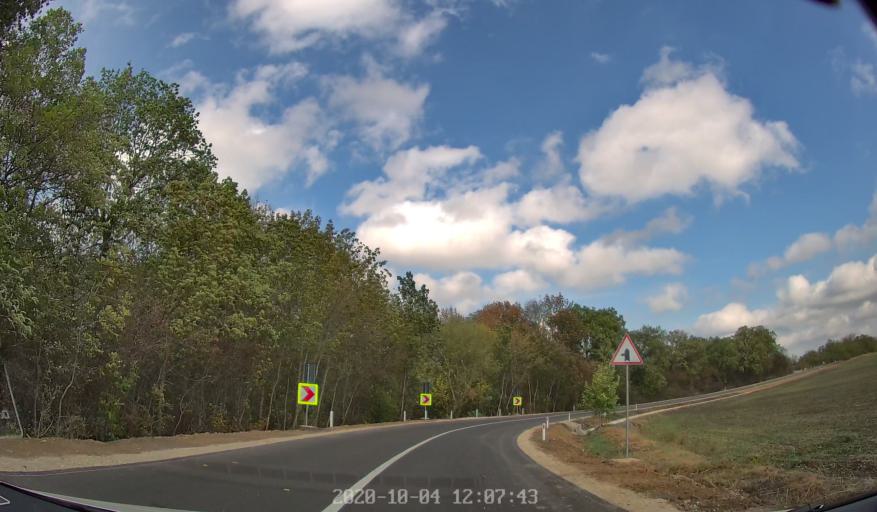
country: MD
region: Rezina
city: Saharna
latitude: 47.5885
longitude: 28.9704
